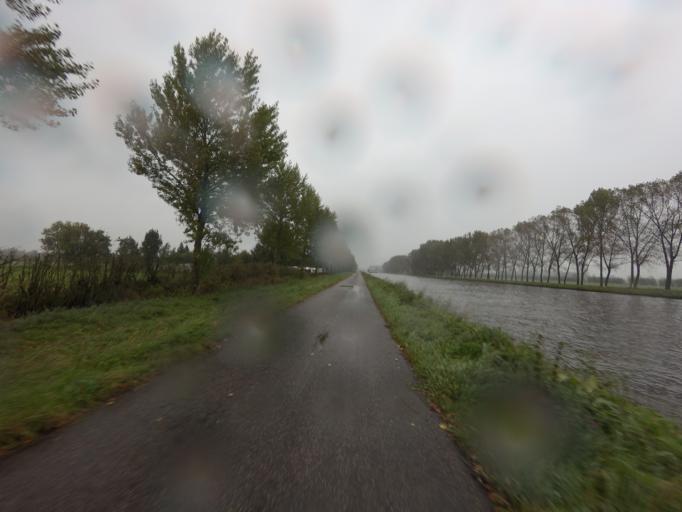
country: NL
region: Utrecht
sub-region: Gemeente Vianen
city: Vianen
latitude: 51.9433
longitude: 5.0463
